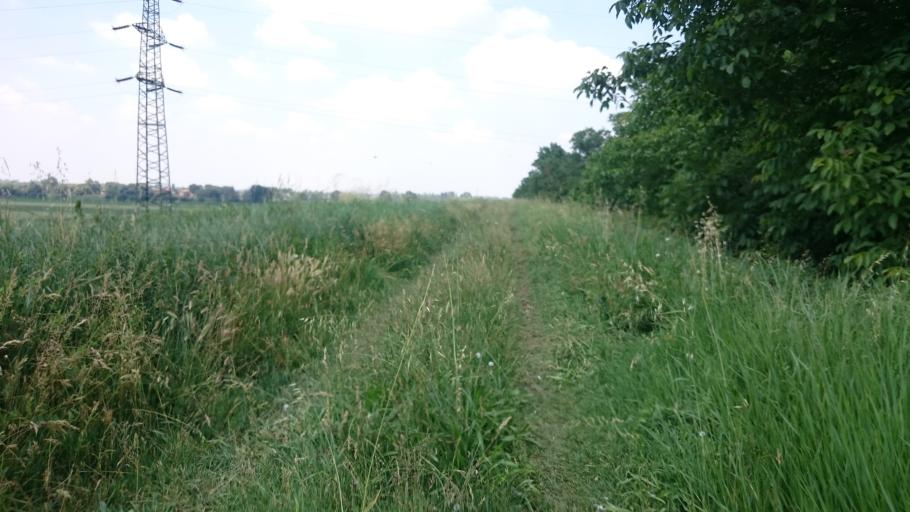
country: IT
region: Lombardy
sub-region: Provincia di Mantova
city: San Biagio
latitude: 45.1126
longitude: 10.8607
